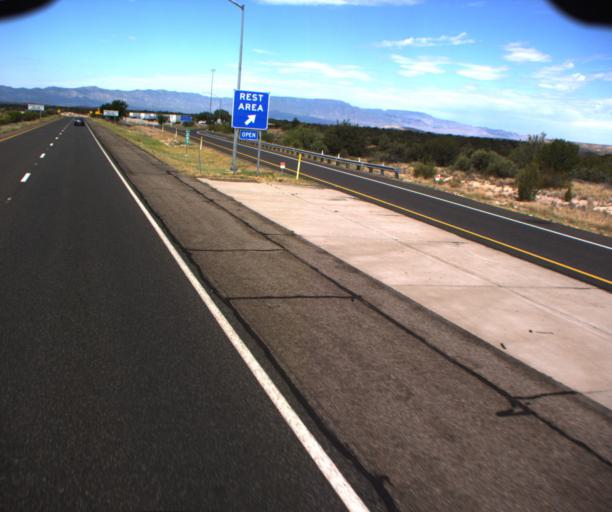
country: US
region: Arizona
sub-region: Yavapai County
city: Lake Montezuma
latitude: 34.6743
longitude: -111.7688
